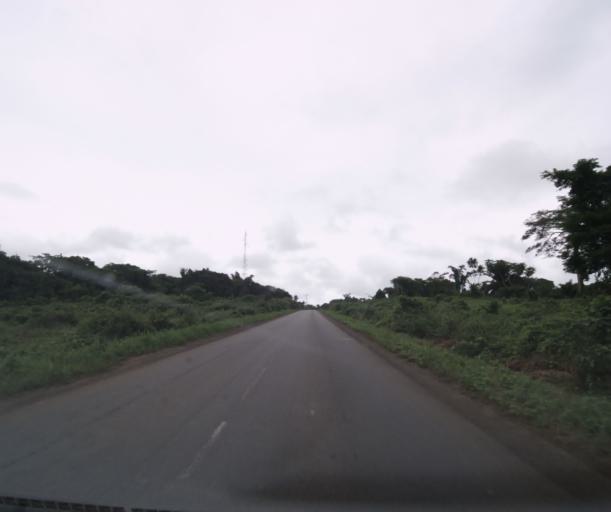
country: CM
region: Littoral
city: Edea
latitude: 3.7171
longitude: 10.1077
